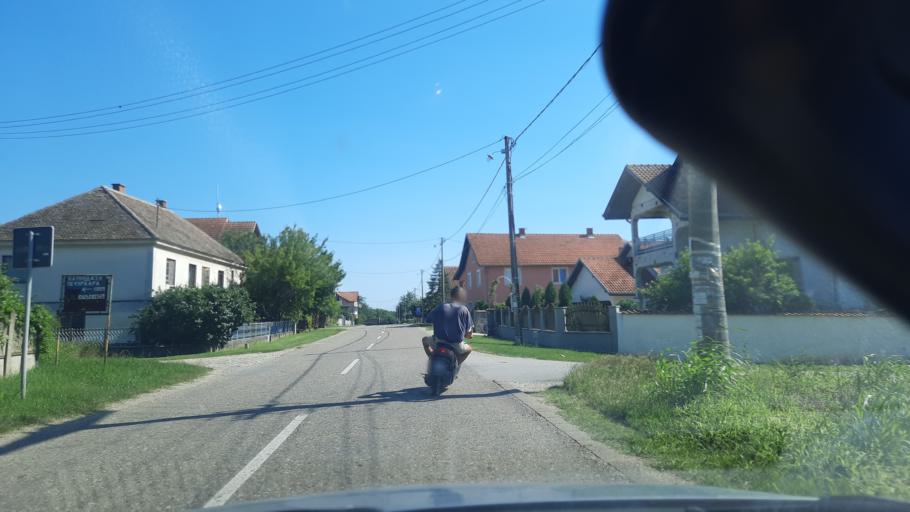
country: RS
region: Central Serbia
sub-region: Branicevski Okrug
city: Malo Crnice
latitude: 44.6117
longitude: 21.2678
